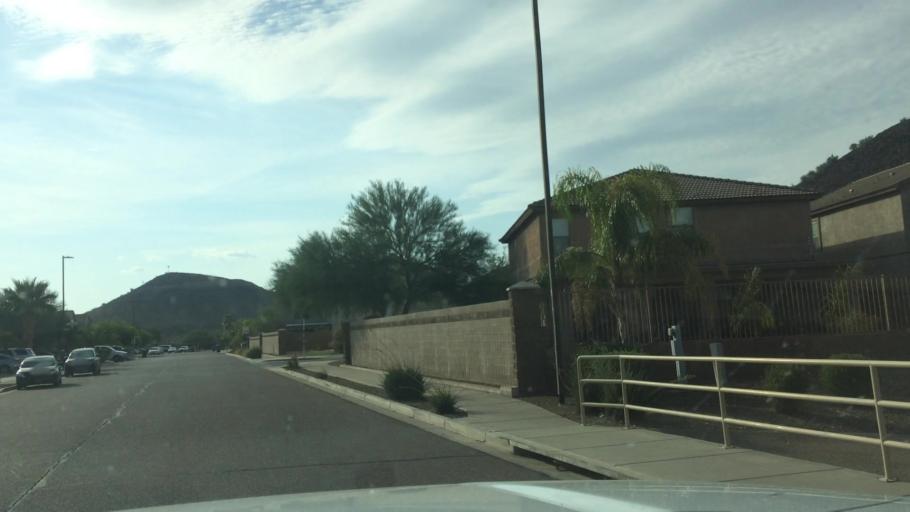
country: US
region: Arizona
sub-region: Maricopa County
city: Cave Creek
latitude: 33.6920
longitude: -112.0427
